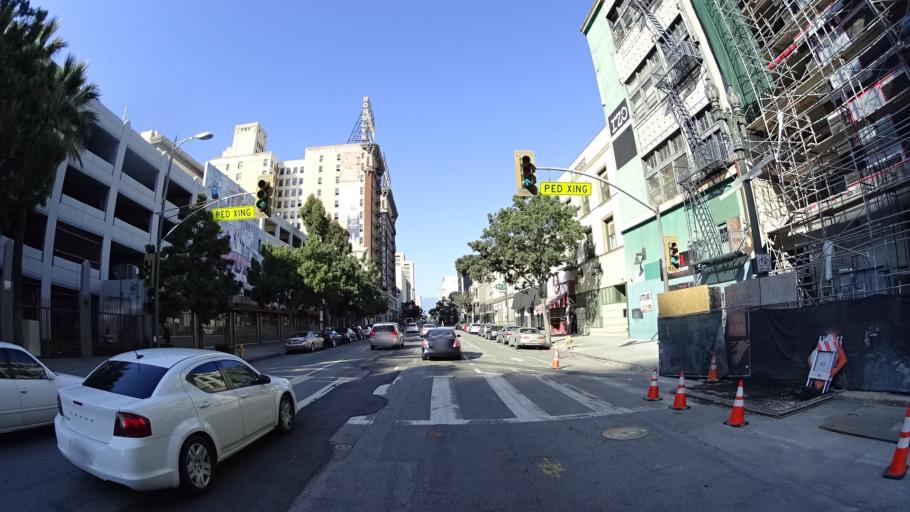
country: US
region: California
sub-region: Los Angeles County
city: Los Angeles
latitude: 34.0458
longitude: -118.2494
